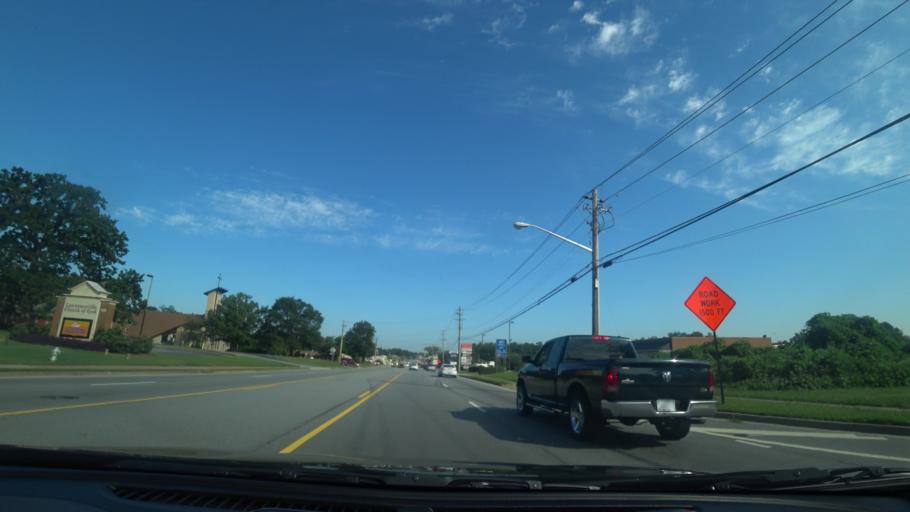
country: US
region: Georgia
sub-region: Gwinnett County
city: Lawrenceville
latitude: 33.9428
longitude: -83.9835
